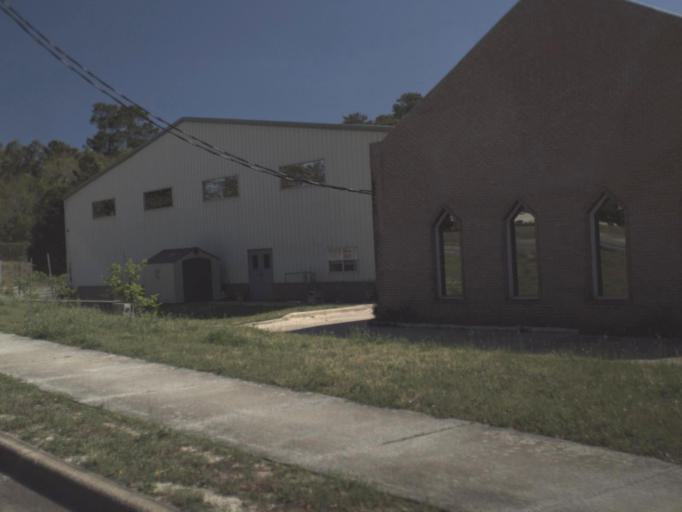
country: US
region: Florida
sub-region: Okaloosa County
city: Ocean City
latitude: 30.4259
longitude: -86.6198
